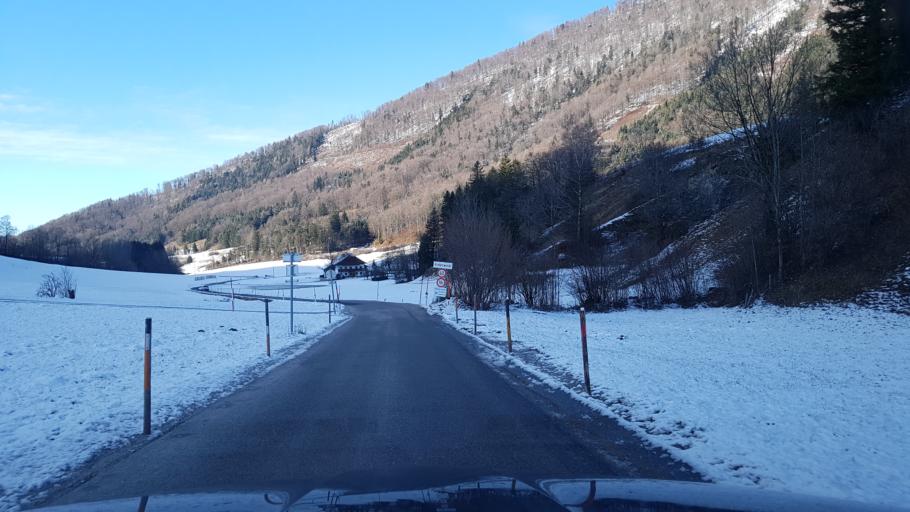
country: AT
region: Salzburg
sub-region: Politischer Bezirk Salzburg-Umgebung
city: Ebenau
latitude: 47.7781
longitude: 13.1543
